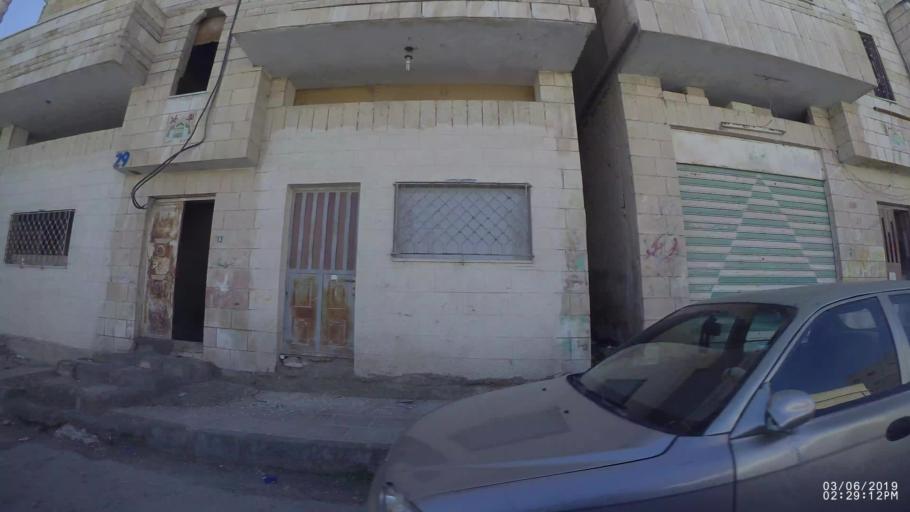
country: JO
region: Zarqa
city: Russeifa
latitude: 32.0349
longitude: 36.0359
